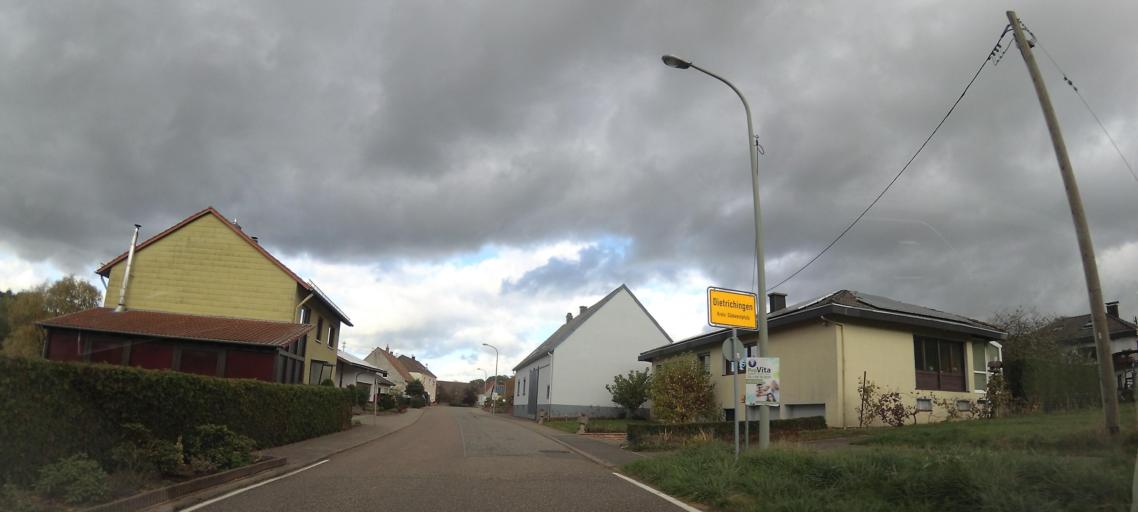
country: DE
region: Rheinland-Pfalz
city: Dietrichingen
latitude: 49.1859
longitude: 7.4133
